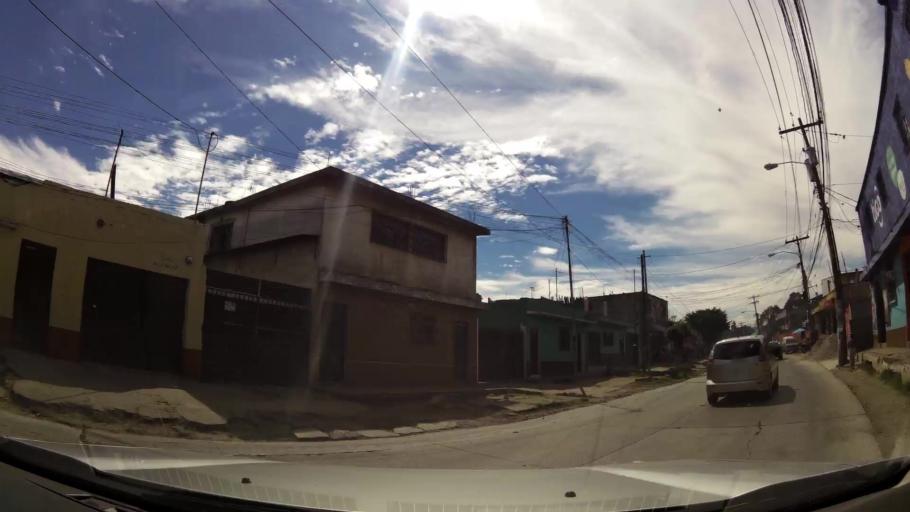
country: GT
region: Guatemala
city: Mixco
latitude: 14.6443
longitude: -90.5948
